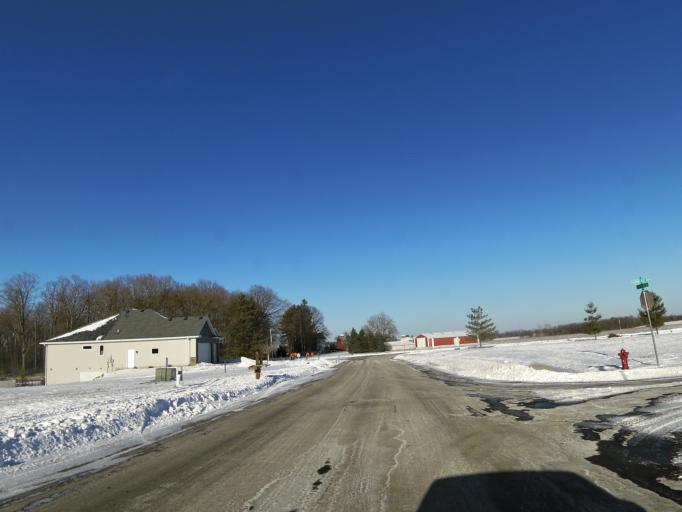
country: US
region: Minnesota
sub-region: Le Sueur County
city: New Prague
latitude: 44.5500
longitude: -93.6003
